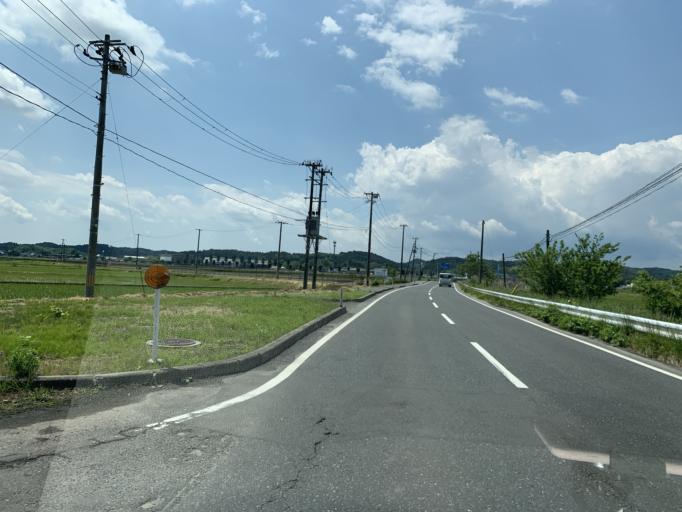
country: JP
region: Miyagi
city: Kogota
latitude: 38.5227
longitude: 141.0576
